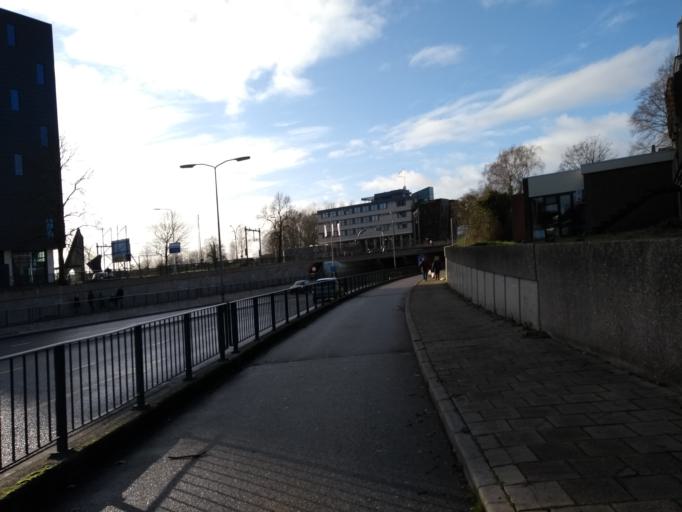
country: NL
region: Overijssel
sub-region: Gemeente Almelo
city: Almelo
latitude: 52.3548
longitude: 6.6601
